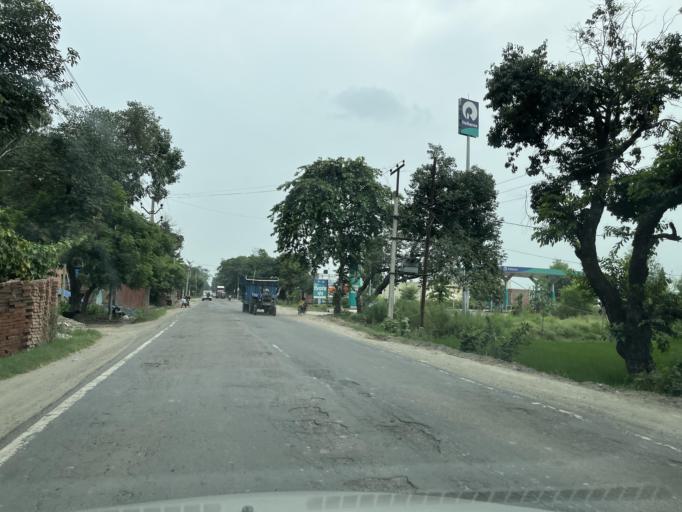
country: IN
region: Uttar Pradesh
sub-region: Rampur
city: Bilaspur
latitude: 29.0309
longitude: 79.2627
